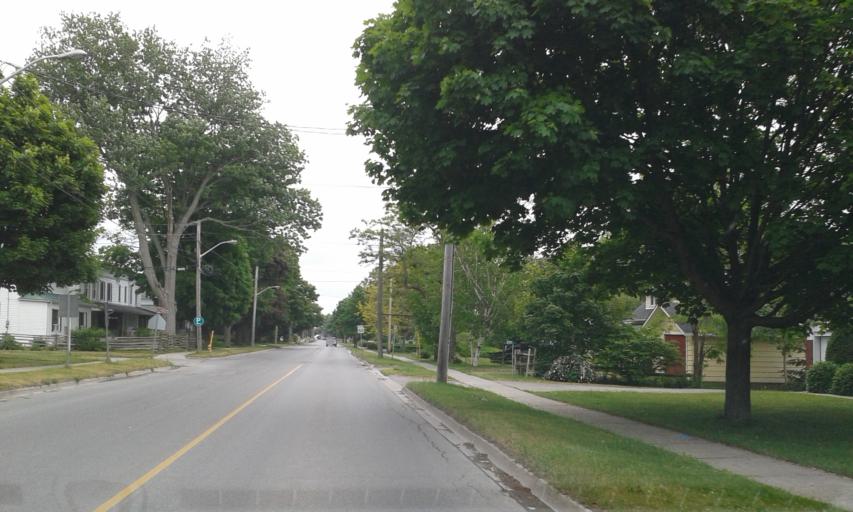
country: CA
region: Ontario
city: Prince Edward
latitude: 43.9517
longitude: -77.3458
